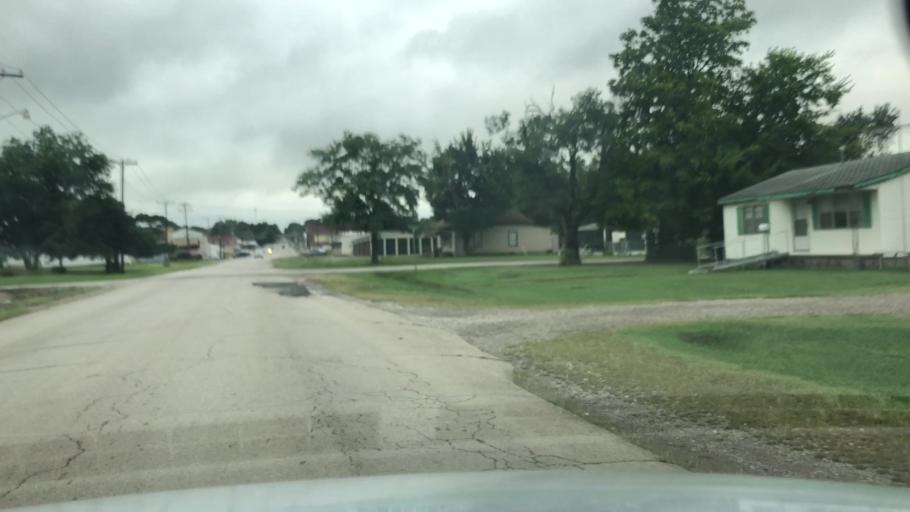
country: US
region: Oklahoma
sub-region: Nowata County
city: Nowata
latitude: 36.7013
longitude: -95.6324
